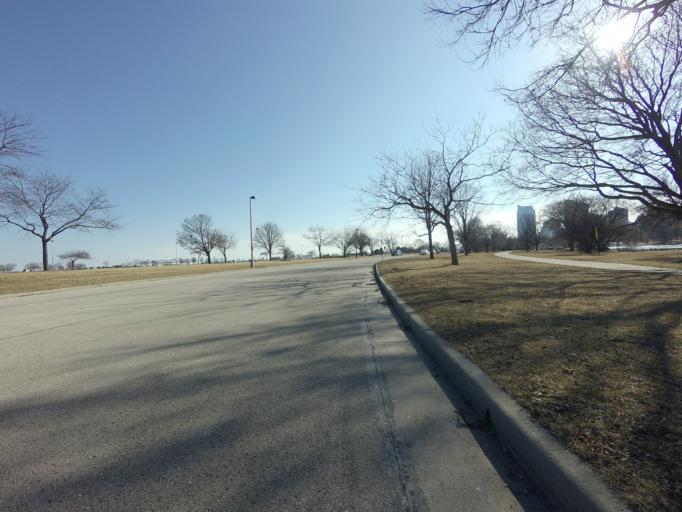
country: US
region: Wisconsin
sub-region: Milwaukee County
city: Milwaukee
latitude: 43.0497
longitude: -87.8895
